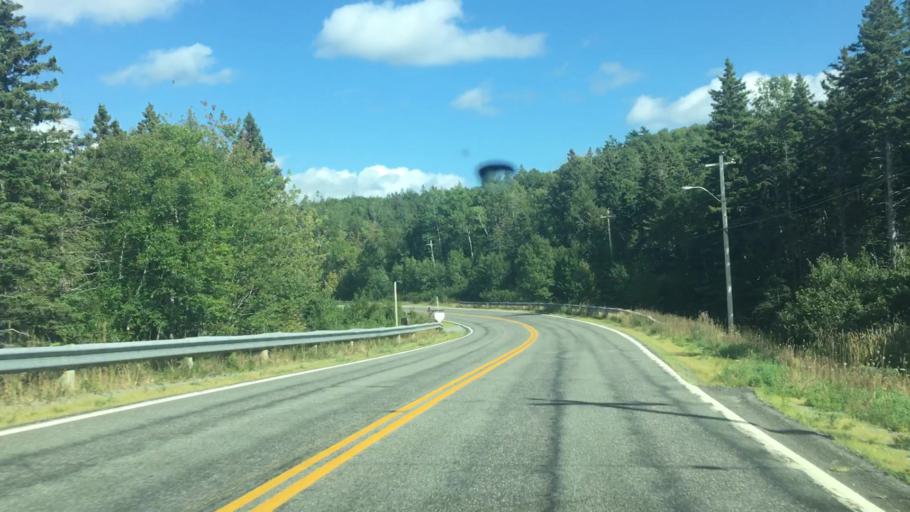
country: CA
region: Nova Scotia
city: Sydney
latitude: 45.8673
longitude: -60.6169
